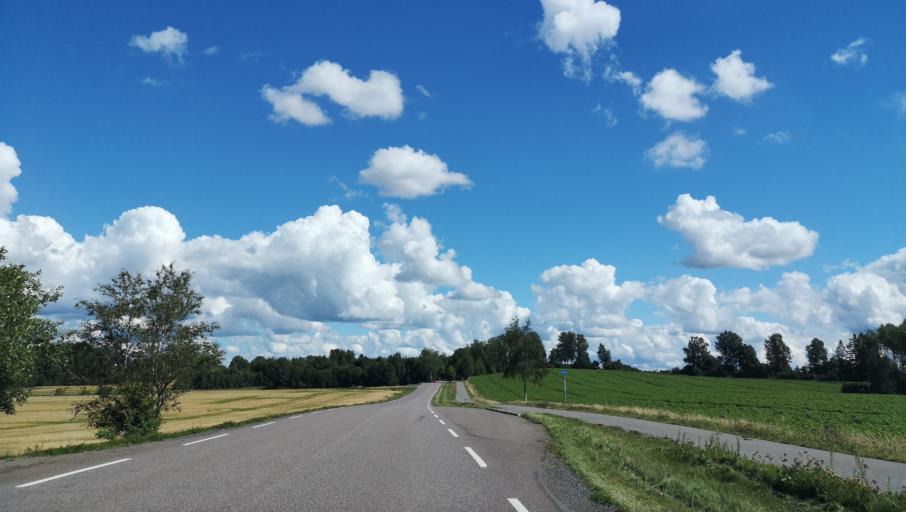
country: NO
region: Akershus
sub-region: Frogn
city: Drobak
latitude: 59.6564
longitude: 10.6944
